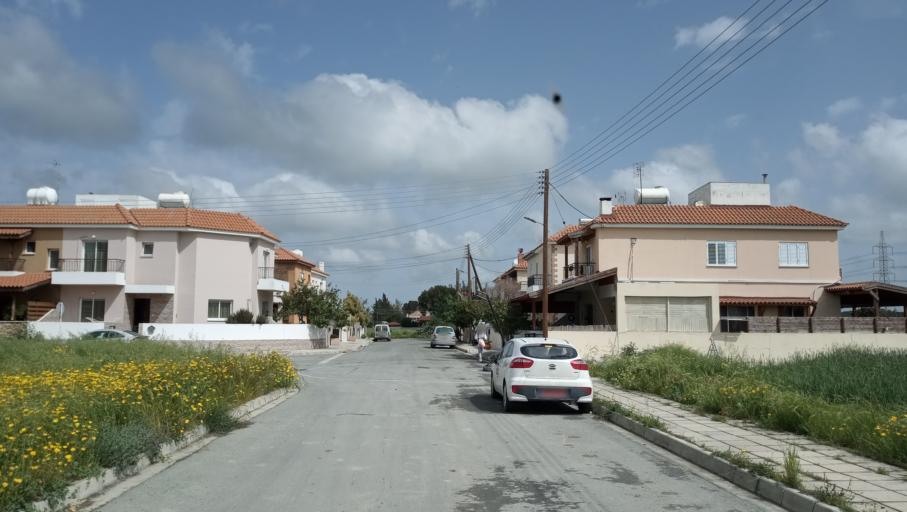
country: CY
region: Lefkosia
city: Dali
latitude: 35.0246
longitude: 33.4336
